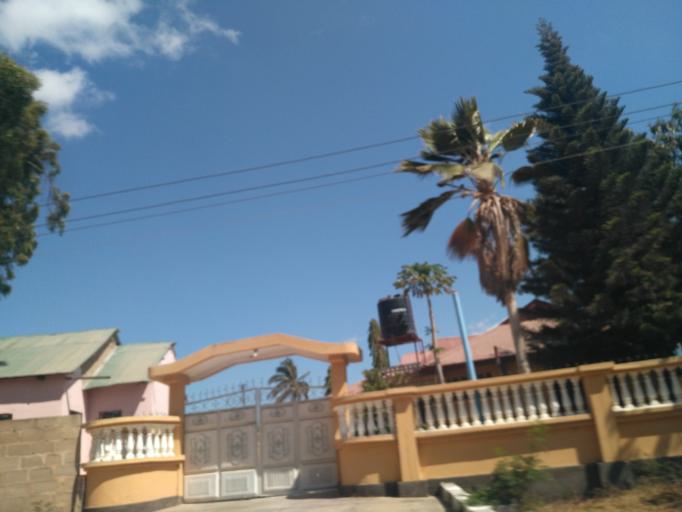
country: TZ
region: Dodoma
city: Dodoma
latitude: -6.1619
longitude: 35.7528
